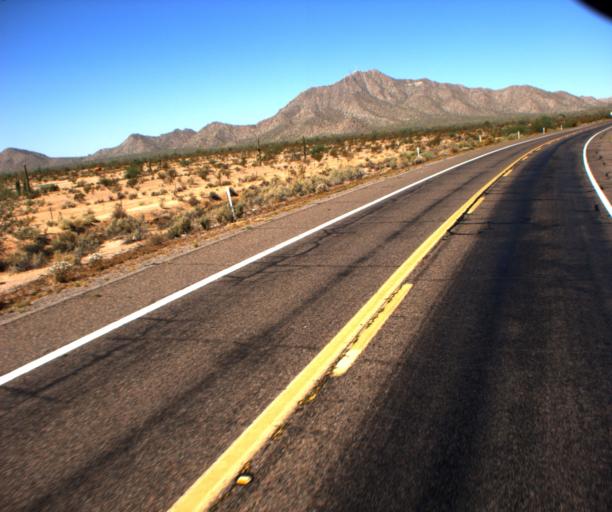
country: US
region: Arizona
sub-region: Pinal County
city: Blackwater
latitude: 33.0193
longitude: -111.6398
